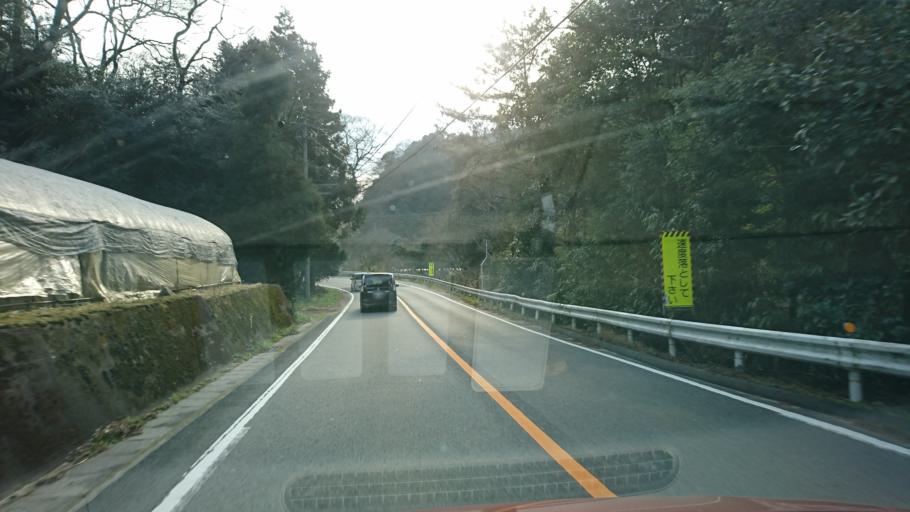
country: JP
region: Ehime
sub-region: Shikoku-chuo Shi
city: Matsuyama
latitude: 33.8961
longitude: 132.8442
